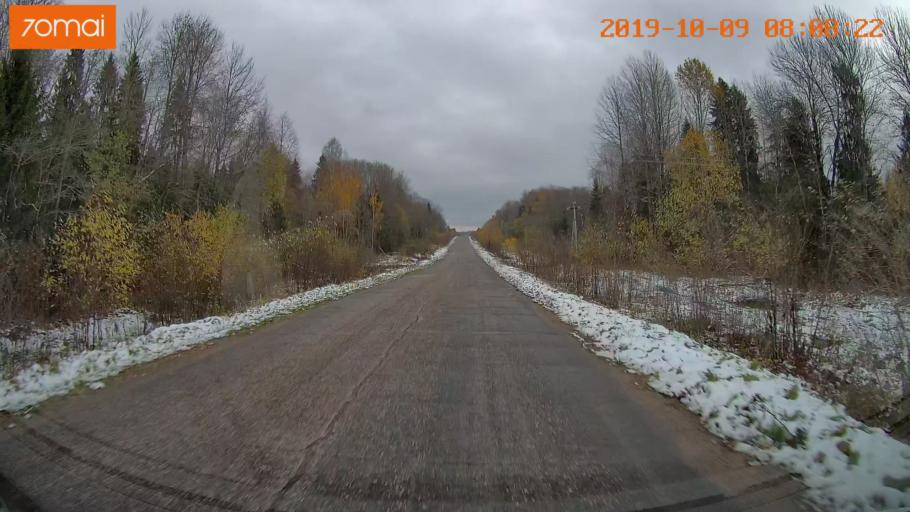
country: RU
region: Jaroslavl
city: Kukoboy
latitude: 58.7038
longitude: 40.0945
